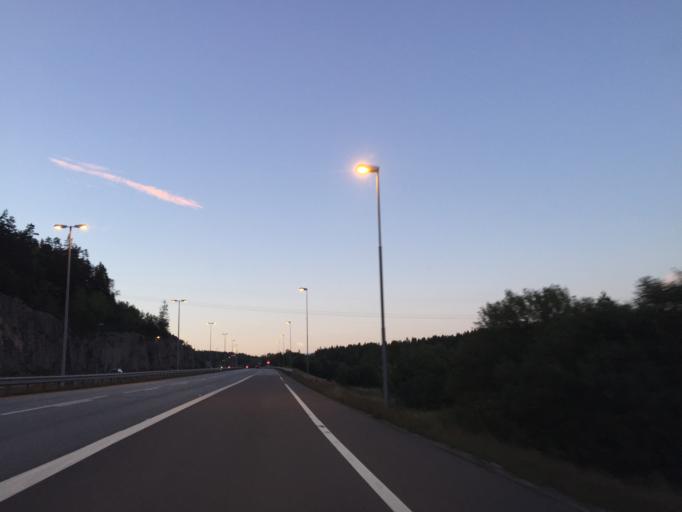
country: NO
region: Akershus
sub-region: Vestby
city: Vestby
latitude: 59.5175
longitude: 10.7258
